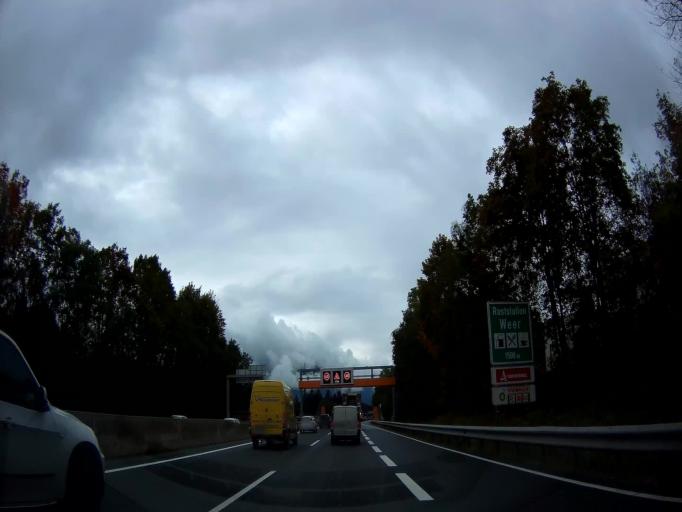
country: AT
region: Tyrol
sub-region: Politischer Bezirk Schwaz
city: Vomp
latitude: 47.3282
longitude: 11.6760
